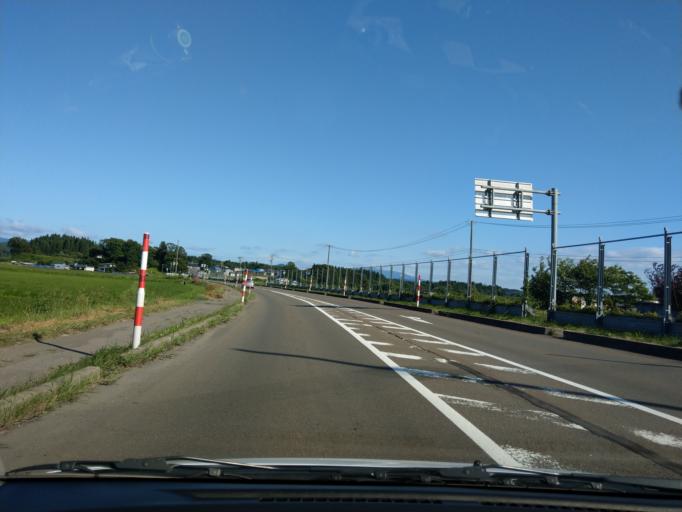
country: JP
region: Akita
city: Takanosu
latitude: 40.1951
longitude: 140.3969
